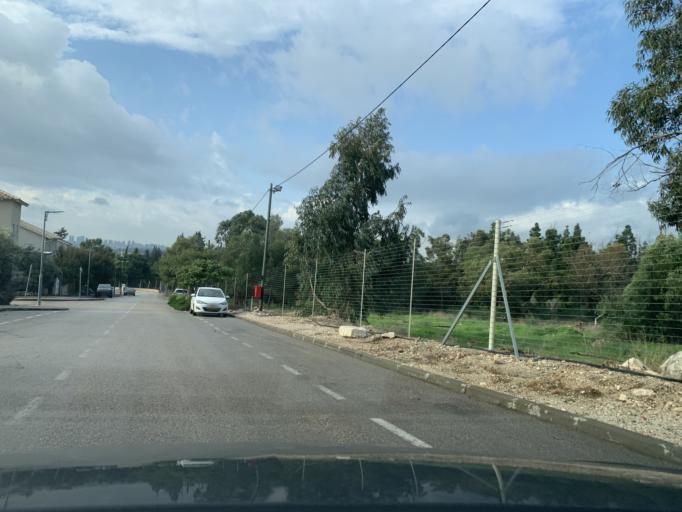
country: IL
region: Central District
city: Rosh Ha'Ayin
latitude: 32.0635
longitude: 34.9508
